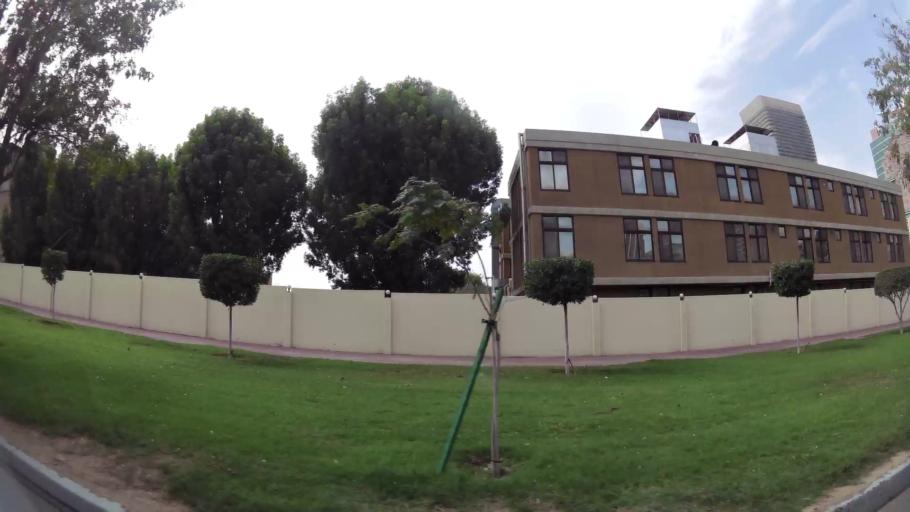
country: AE
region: Abu Dhabi
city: Abu Dhabi
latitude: 24.4682
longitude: 54.3440
